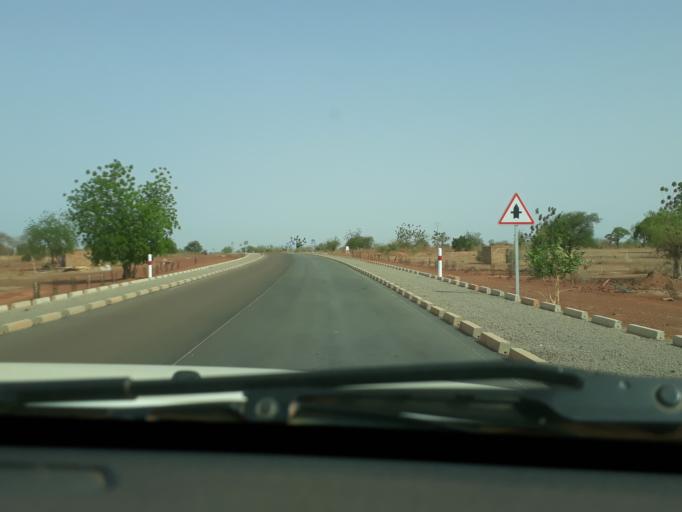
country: BF
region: Plateau-Central
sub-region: Province d'Oubritenga
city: Ziniare
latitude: 12.5488
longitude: -1.3890
